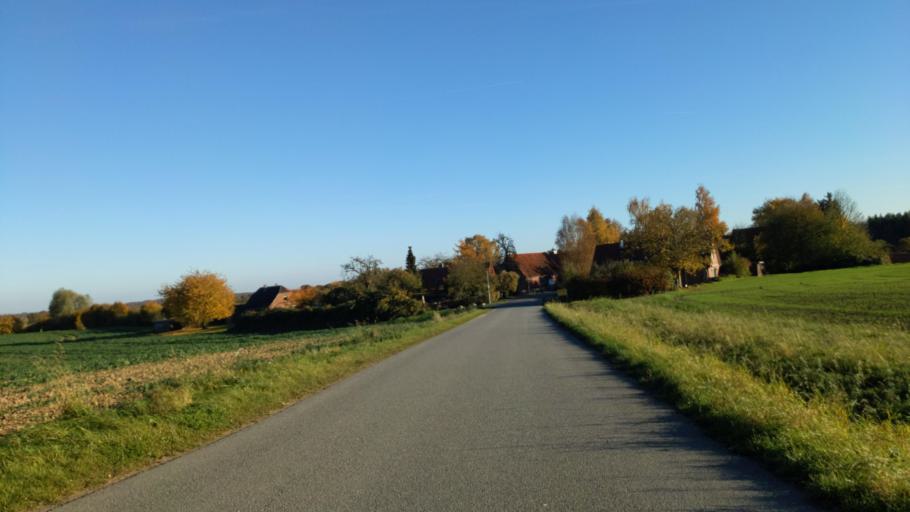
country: DE
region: Schleswig-Holstein
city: Pogeez
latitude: 53.7346
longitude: 10.7098
